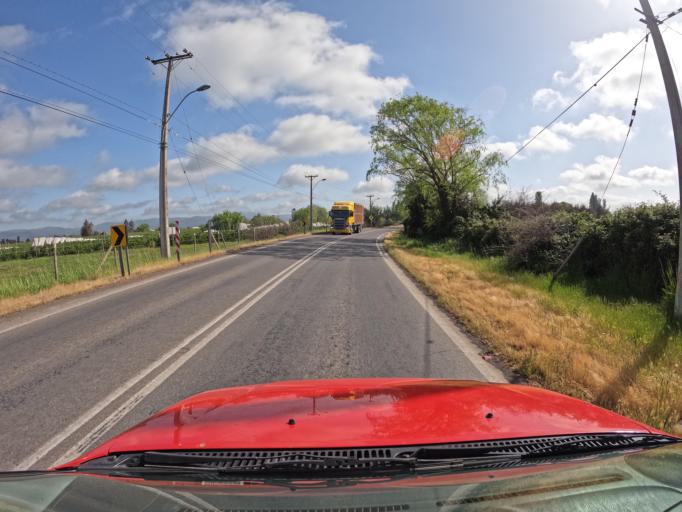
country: CL
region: Maule
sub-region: Provincia de Curico
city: Rauco
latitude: -34.8908
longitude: -71.2742
